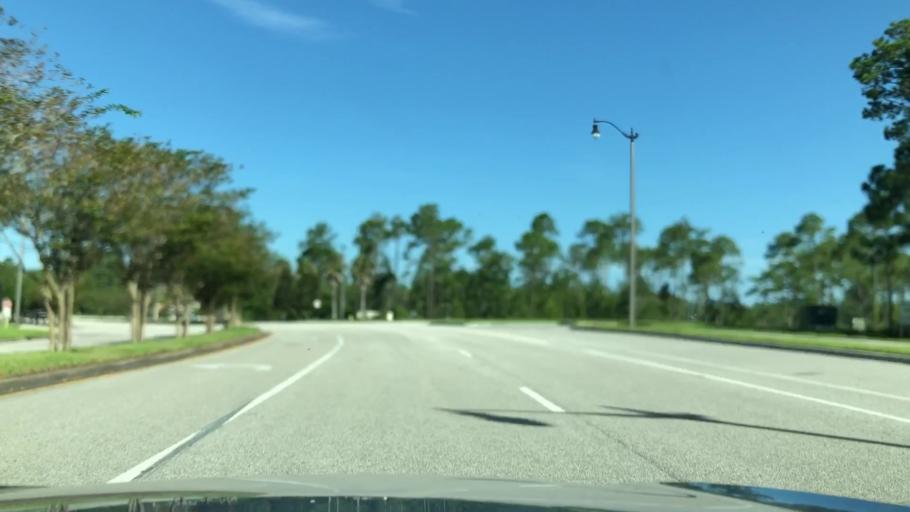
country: US
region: Florida
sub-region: Saint Johns County
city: Palm Valley
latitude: 30.1063
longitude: -81.4315
